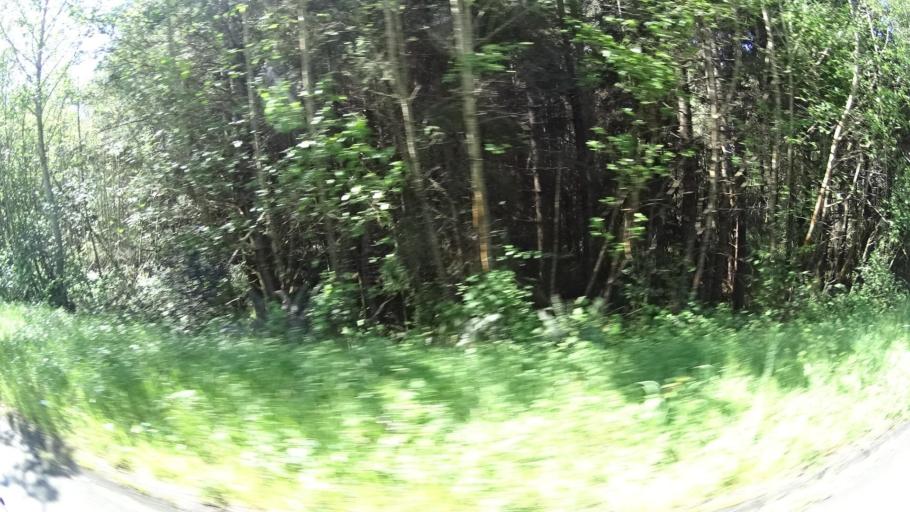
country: US
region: California
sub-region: Humboldt County
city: McKinleyville
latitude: 40.9568
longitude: -124.0892
